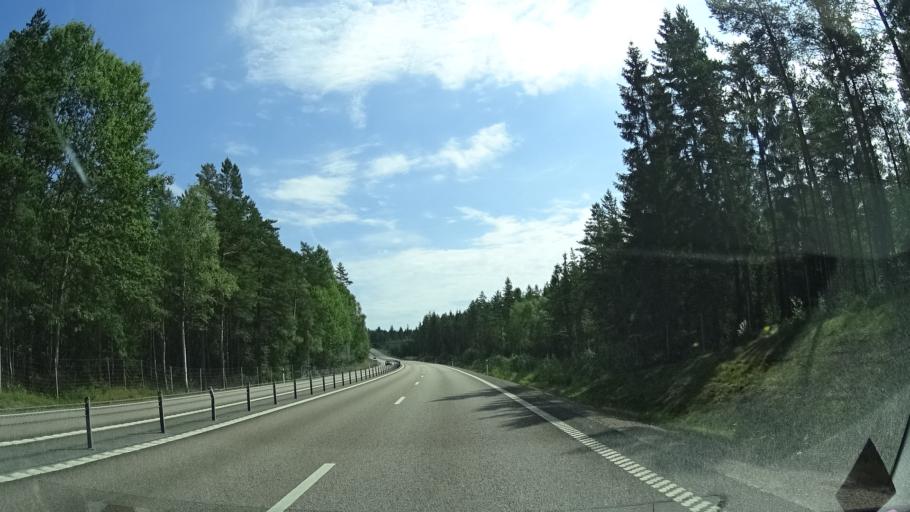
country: SE
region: Vaermland
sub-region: Kristinehamns Kommun
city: Kristinehamn
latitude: 59.3133
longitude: 14.1639
